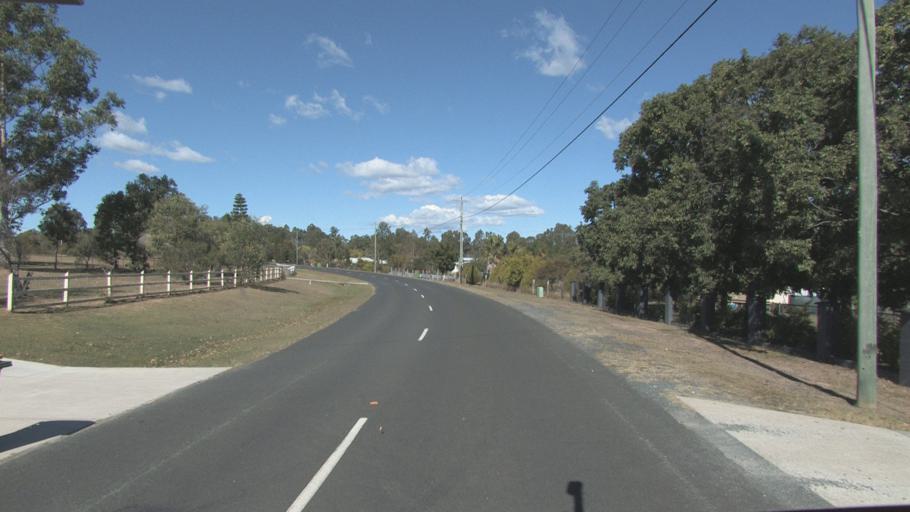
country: AU
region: Queensland
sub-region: Logan
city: North Maclean
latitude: -27.7407
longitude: 152.9461
